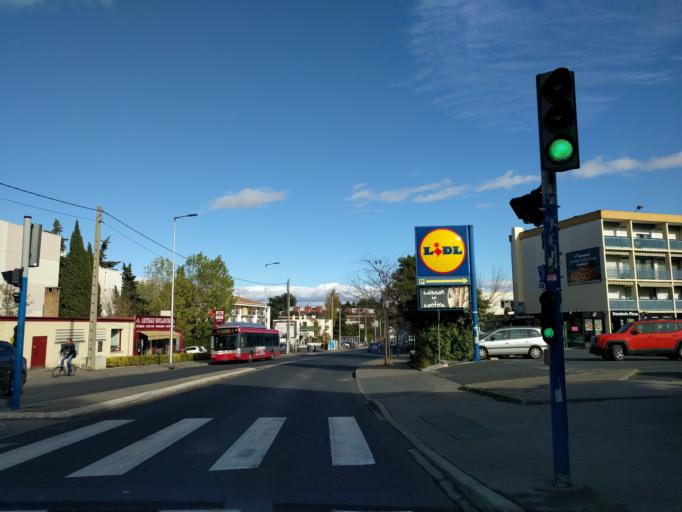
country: FR
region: Languedoc-Roussillon
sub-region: Departement de l'Herault
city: Montpellier
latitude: 43.6182
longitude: 3.8444
